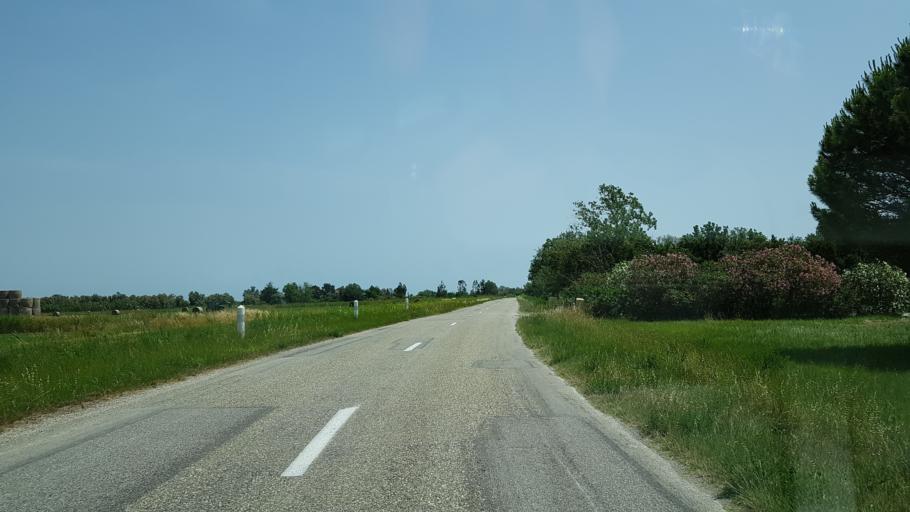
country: FR
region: Provence-Alpes-Cote d'Azur
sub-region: Departement des Bouches-du-Rhone
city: Port-Saint-Louis-du-Rhone
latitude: 43.4317
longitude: 4.6899
